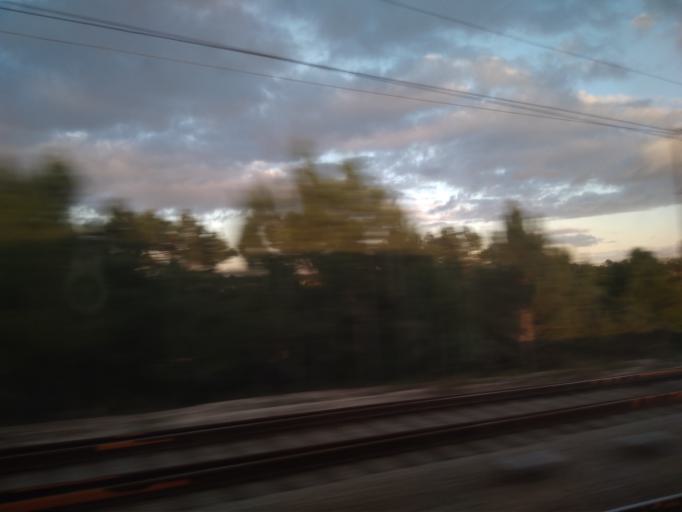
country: PT
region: Setubal
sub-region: Seixal
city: Aldeia de Paio Pires
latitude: 38.5981
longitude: -9.0782
